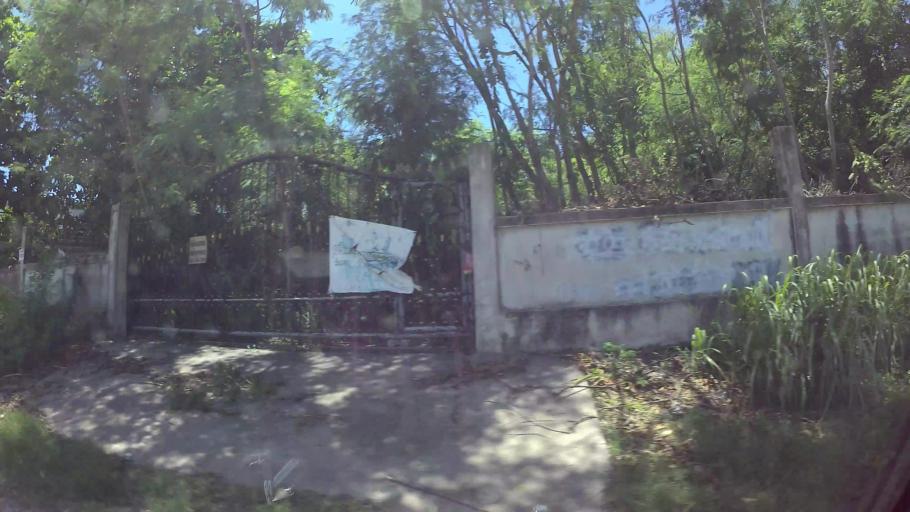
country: TH
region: Chon Buri
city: Phatthaya
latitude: 12.9228
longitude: 100.8970
